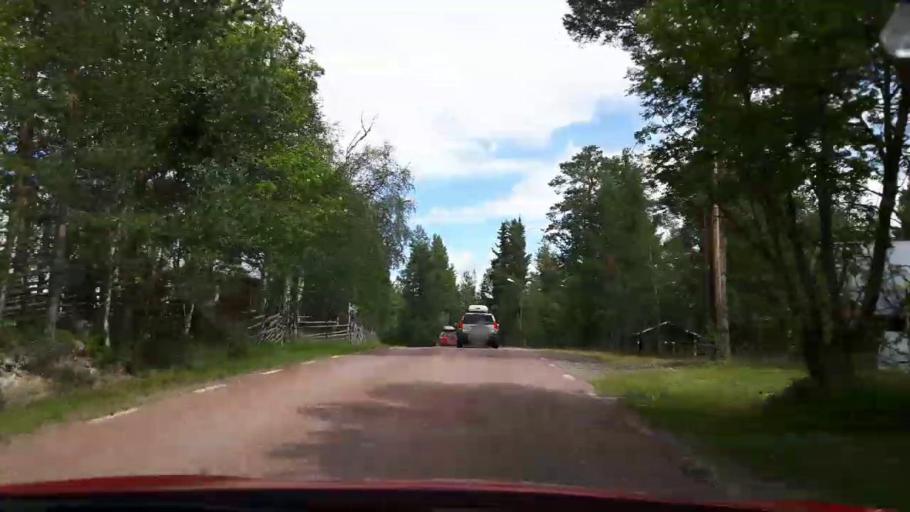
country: NO
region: Hedmark
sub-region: Trysil
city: Innbygda
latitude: 61.8336
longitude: 12.9547
